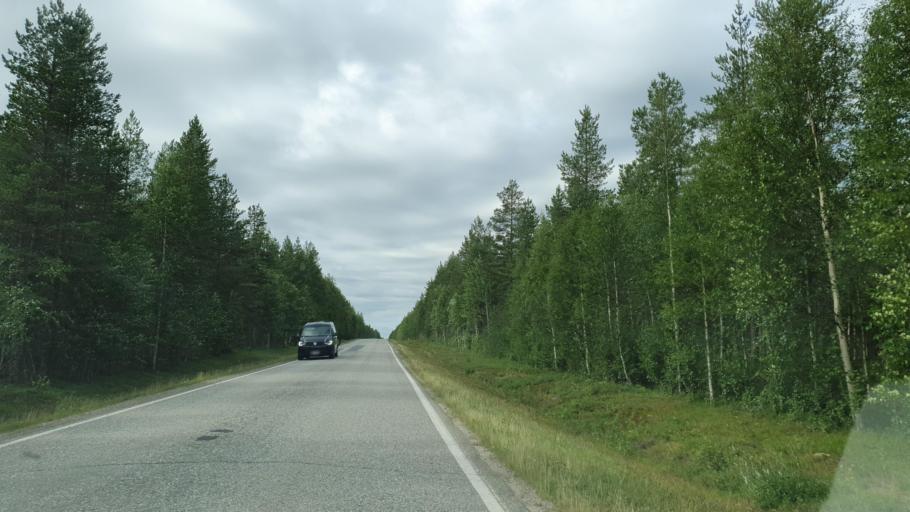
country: FI
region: Lapland
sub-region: Tunturi-Lappi
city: Kittilae
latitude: 67.6127
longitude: 25.3100
